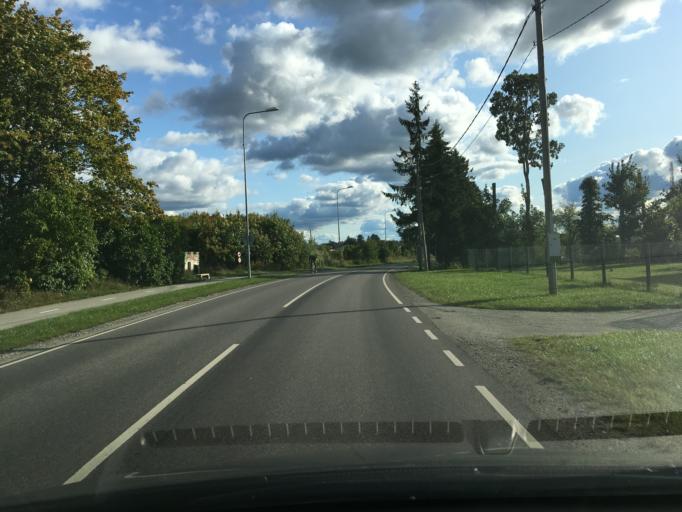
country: EE
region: Harju
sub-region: Joelaehtme vald
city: Loo
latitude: 59.4122
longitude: 24.9477
